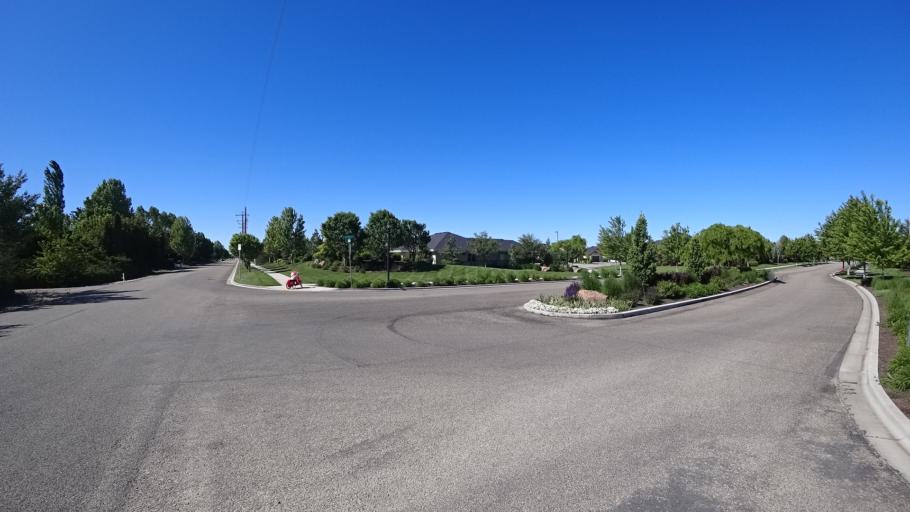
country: US
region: Idaho
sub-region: Ada County
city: Eagle
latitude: 43.6673
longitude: -116.3936
